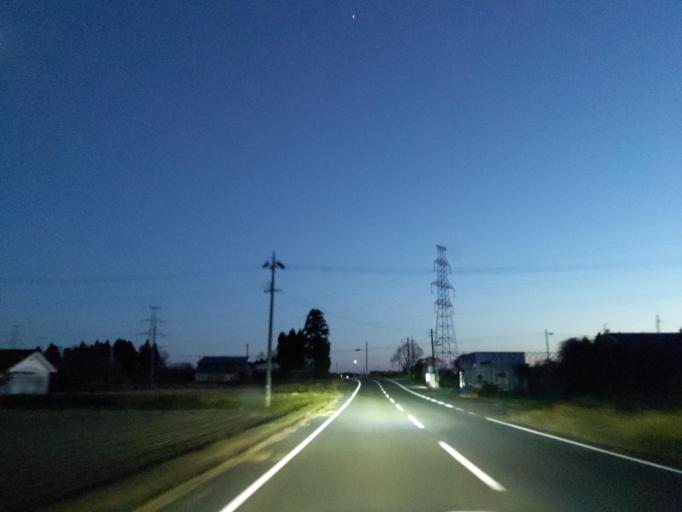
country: JP
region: Fukushima
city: Sukagawa
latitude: 37.3277
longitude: 140.3886
